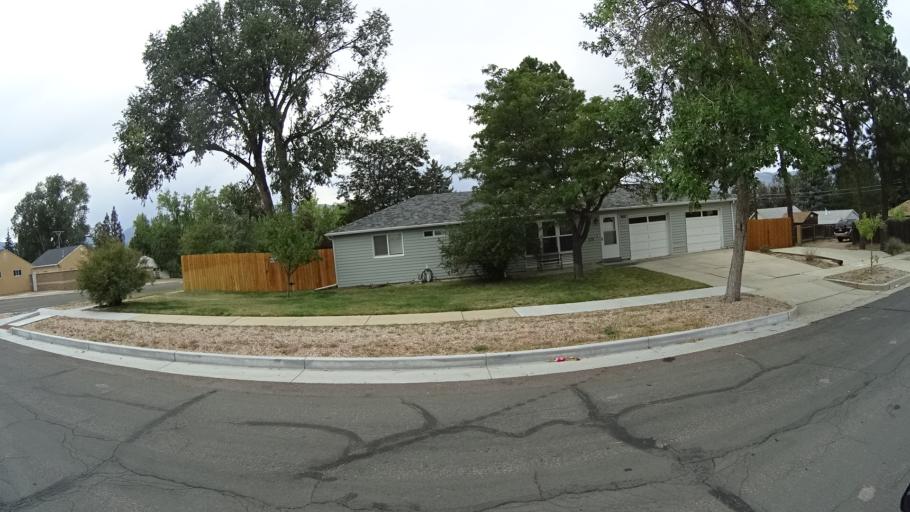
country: US
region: Colorado
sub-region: El Paso County
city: Colorado Springs
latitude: 38.8646
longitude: -104.7896
